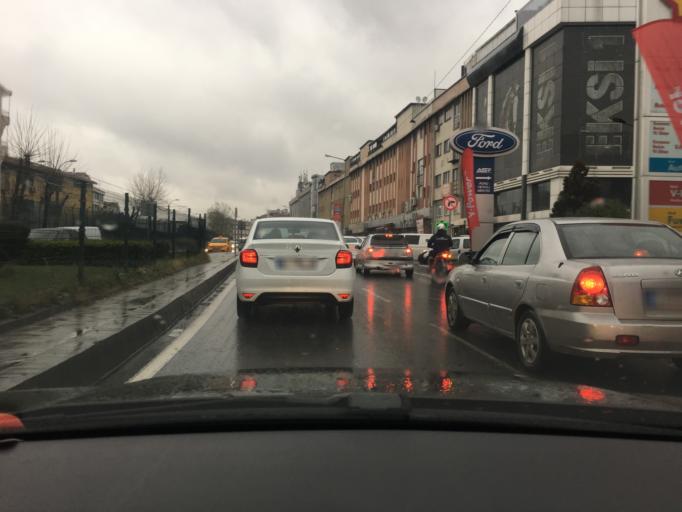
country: TR
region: Istanbul
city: merter keresteciler
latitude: 41.0281
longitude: 28.8992
